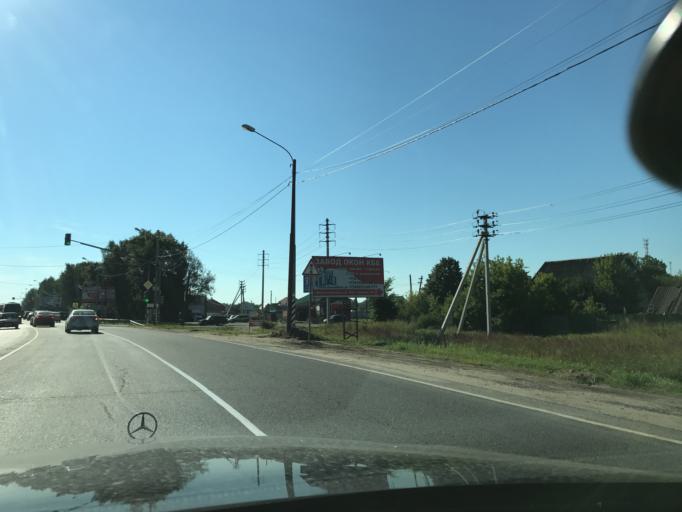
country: RU
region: Moskovskaya
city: Noginsk-9
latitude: 56.1095
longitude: 38.6196
